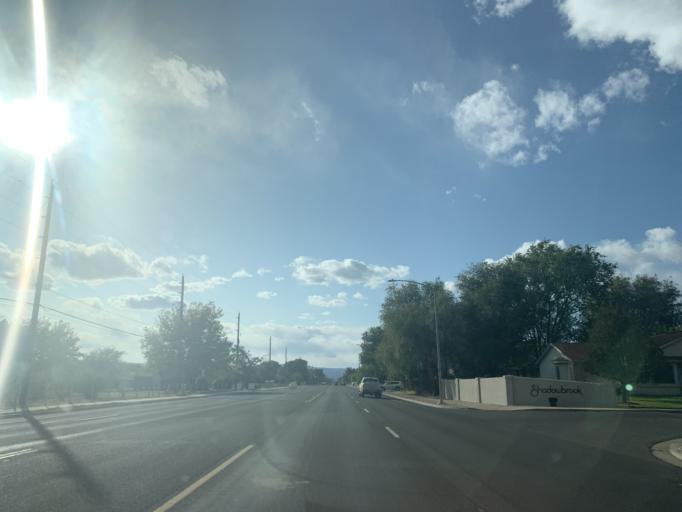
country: US
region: Colorado
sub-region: Mesa County
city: Fruitvale
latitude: 39.0918
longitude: -108.4820
